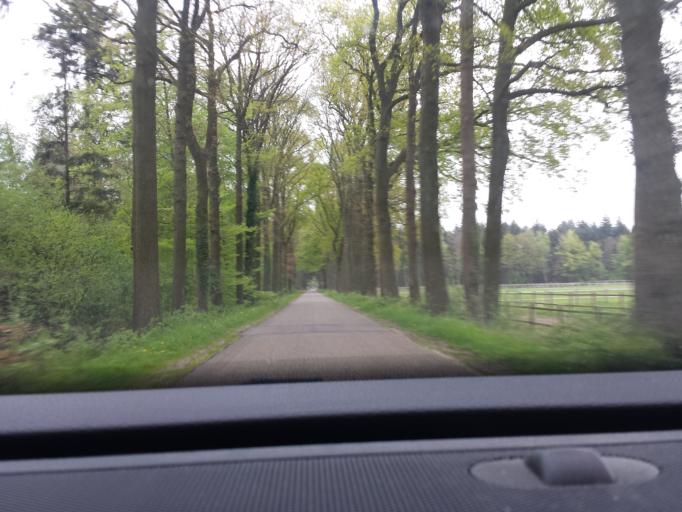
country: NL
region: Gelderland
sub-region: Gemeente Bronckhorst
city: Hengelo
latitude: 52.0951
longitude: 6.3417
